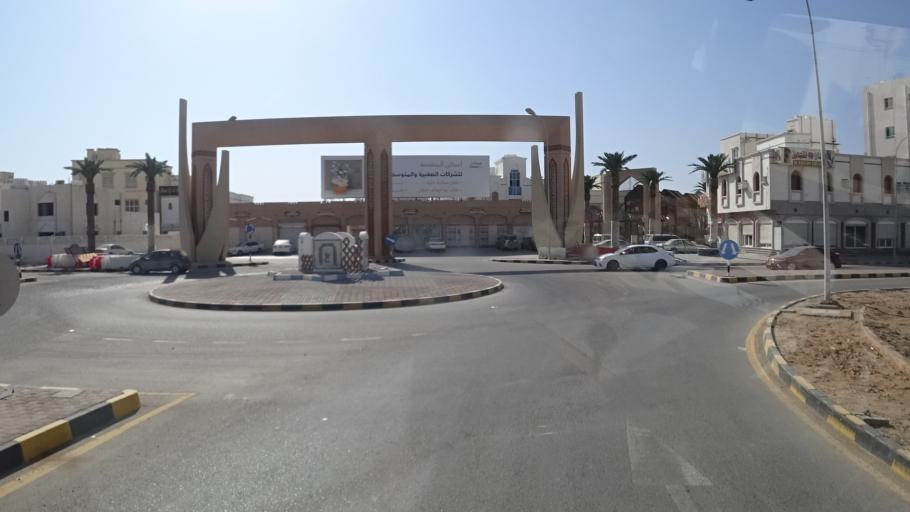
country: OM
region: Ash Sharqiyah
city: Sur
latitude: 22.5717
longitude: 59.5264
